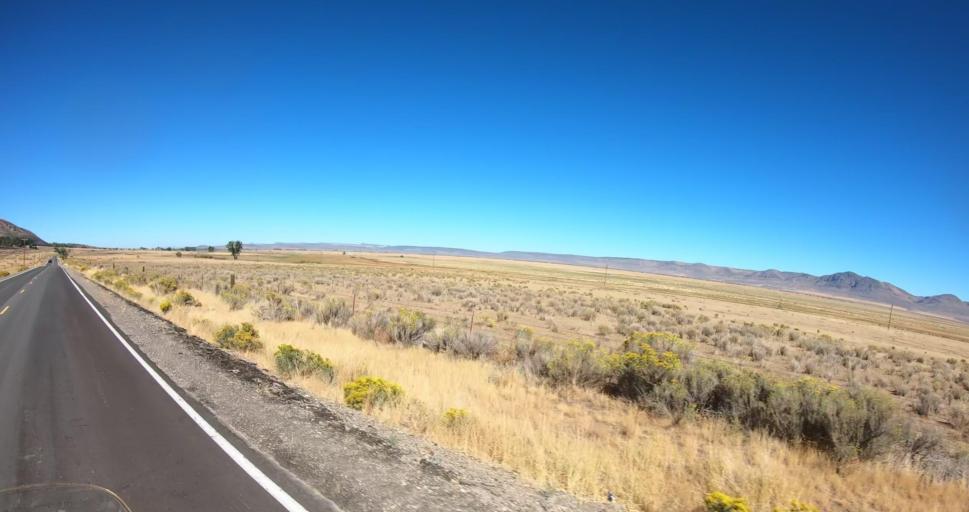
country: US
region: Oregon
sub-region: Lake County
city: Lakeview
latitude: 42.6319
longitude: -120.5129
